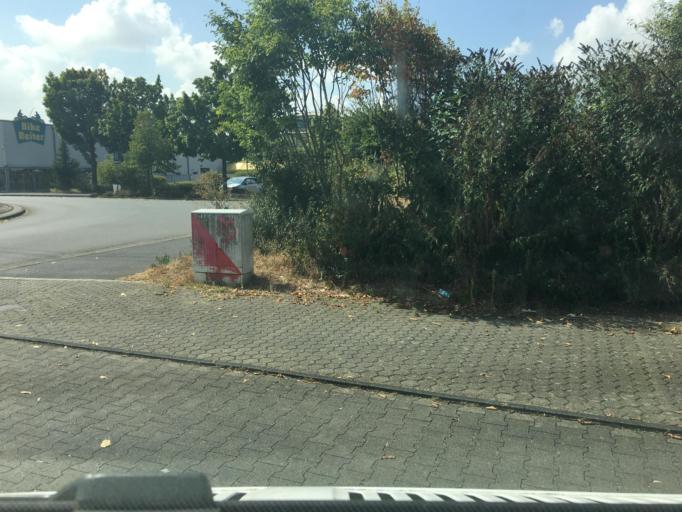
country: DE
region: North Rhine-Westphalia
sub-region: Regierungsbezirk Koln
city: Erftstadt
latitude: 50.7986
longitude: 6.7813
